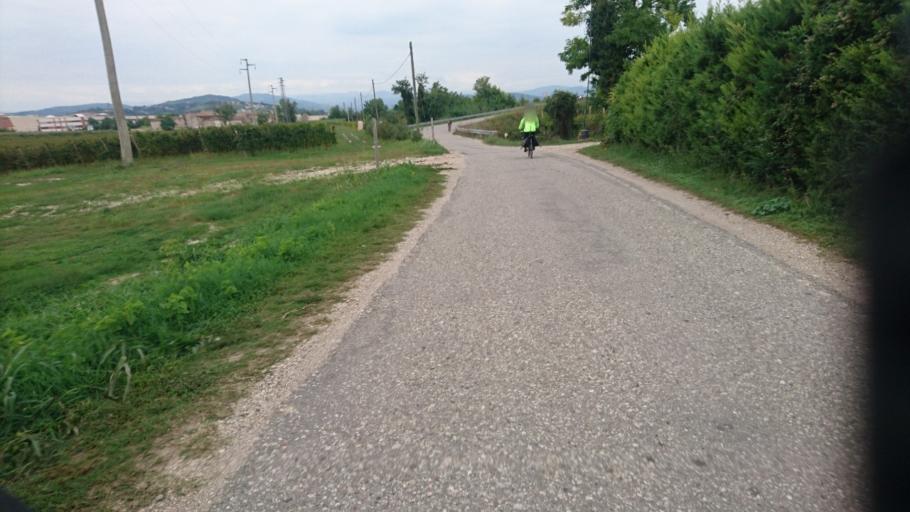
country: IT
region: Veneto
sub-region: Provincia di Verona
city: Caldierino-Rota
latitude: 45.4056
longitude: 11.1421
